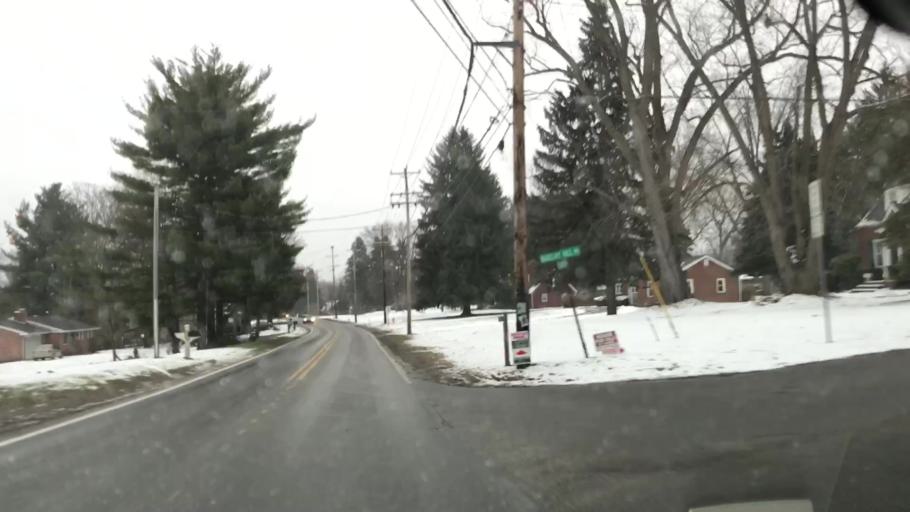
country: US
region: Pennsylvania
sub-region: Beaver County
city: Industry
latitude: 40.6973
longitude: -80.3891
